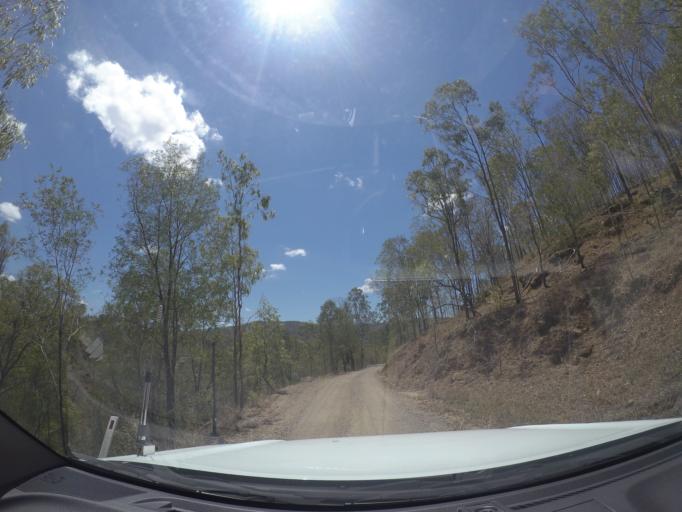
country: AU
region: Queensland
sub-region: Ipswich
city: Springfield Lakes
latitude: -27.8166
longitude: 152.8491
